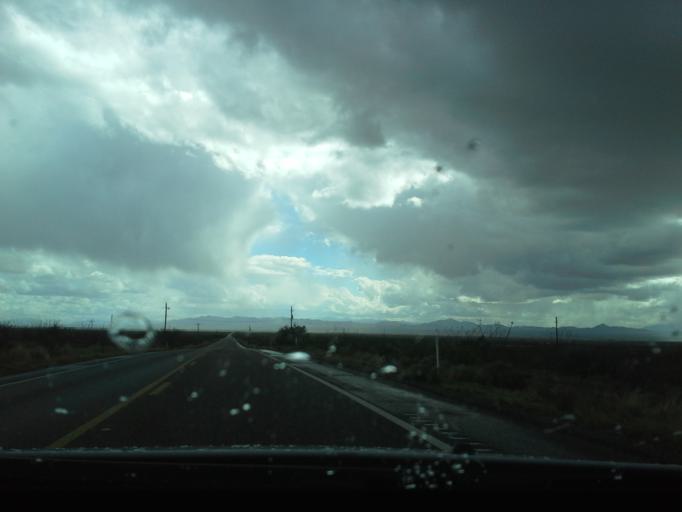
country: US
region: Arizona
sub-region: Cochise County
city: Douglas
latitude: 31.4411
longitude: -109.4764
